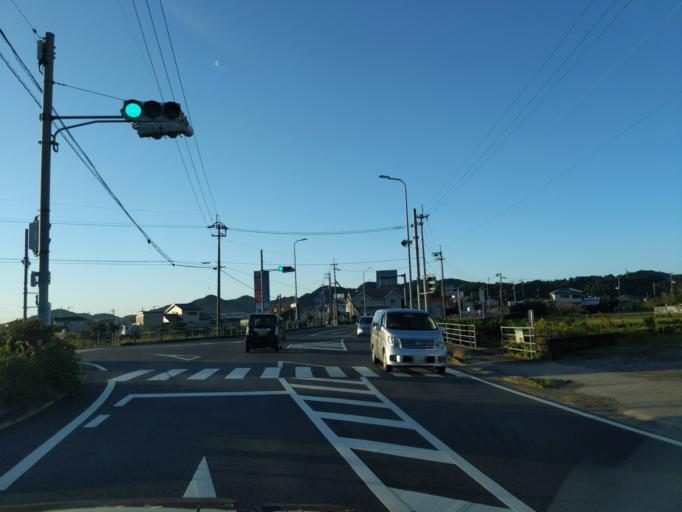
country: JP
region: Kochi
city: Muroto-misakicho
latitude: 33.6127
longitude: 134.3534
